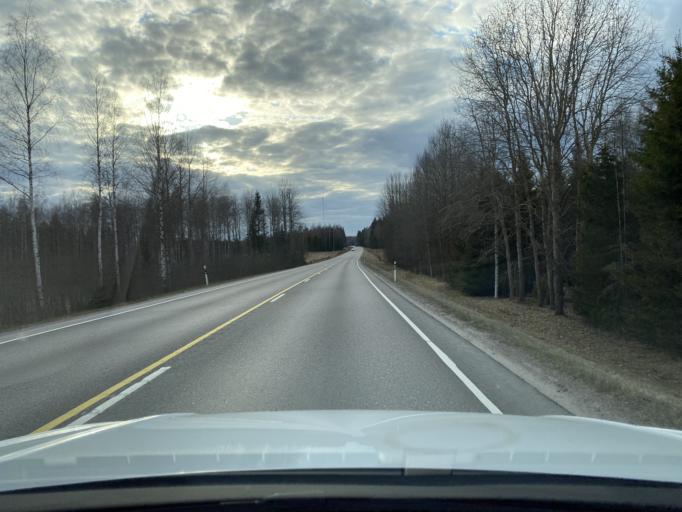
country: FI
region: Haeme
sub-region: Haemeenlinna
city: Renko
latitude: 60.7836
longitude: 24.1529
